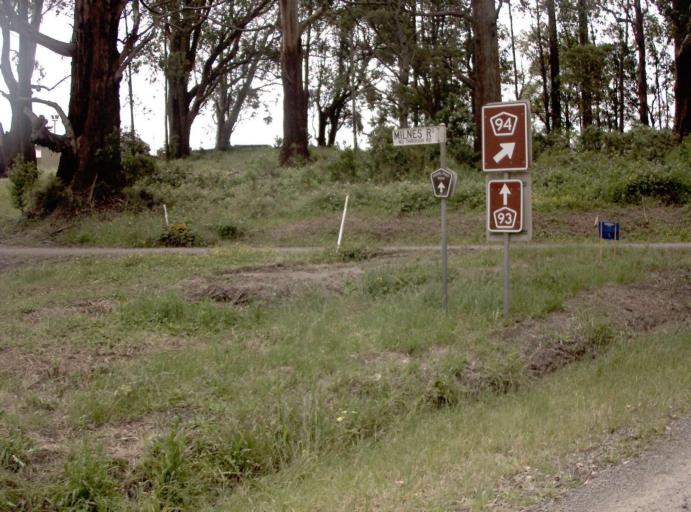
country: AU
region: Victoria
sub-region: Latrobe
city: Traralgon
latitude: -38.3801
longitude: 146.6676
